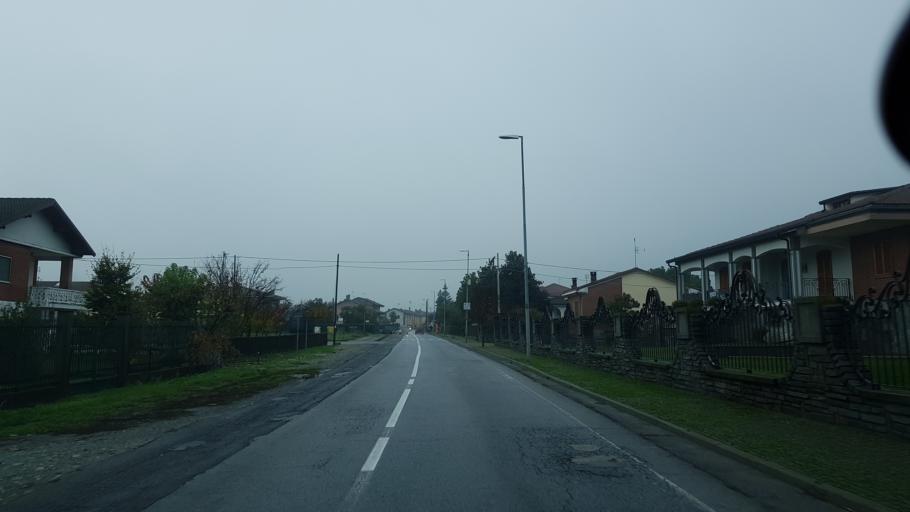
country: IT
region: Piedmont
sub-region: Provincia di Cuneo
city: Vottignasco
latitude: 44.5652
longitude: 7.5840
